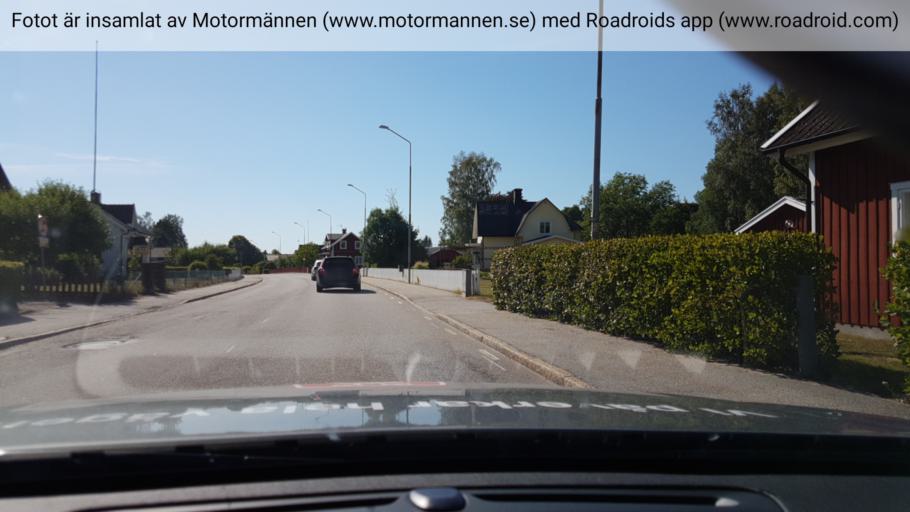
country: SE
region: Vaestra Goetaland
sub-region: Toreboda Kommun
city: Toereboda
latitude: 58.7105
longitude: 14.1464
